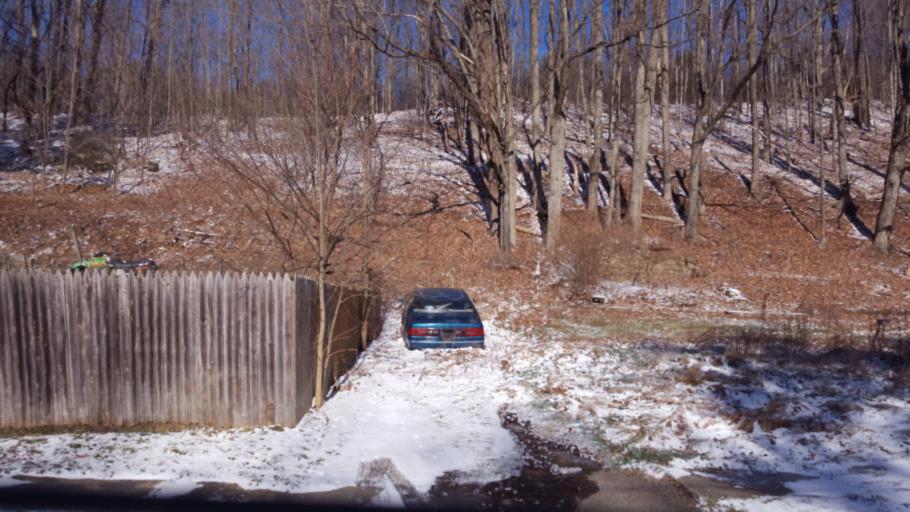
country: US
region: New York
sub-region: Allegany County
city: Wellsville
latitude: 42.1277
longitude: -77.9409
